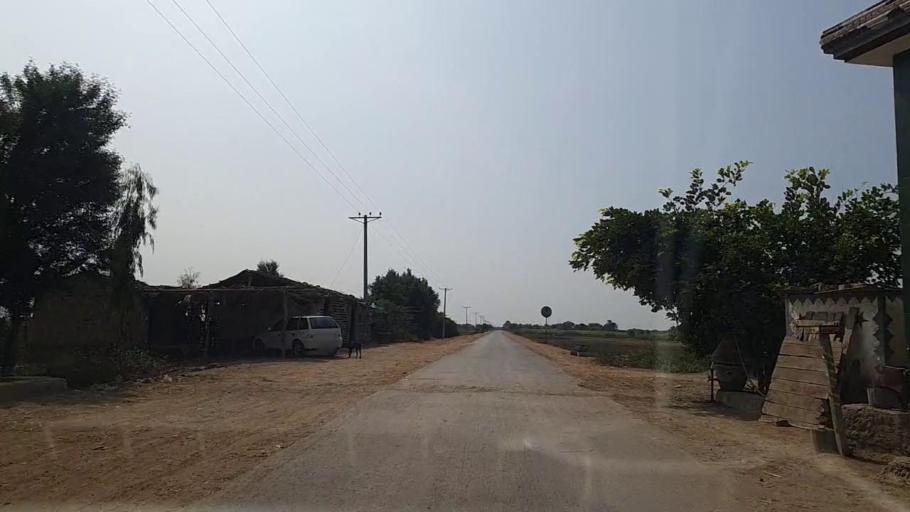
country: PK
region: Sindh
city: Chuhar Jamali
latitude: 24.3579
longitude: 67.9583
